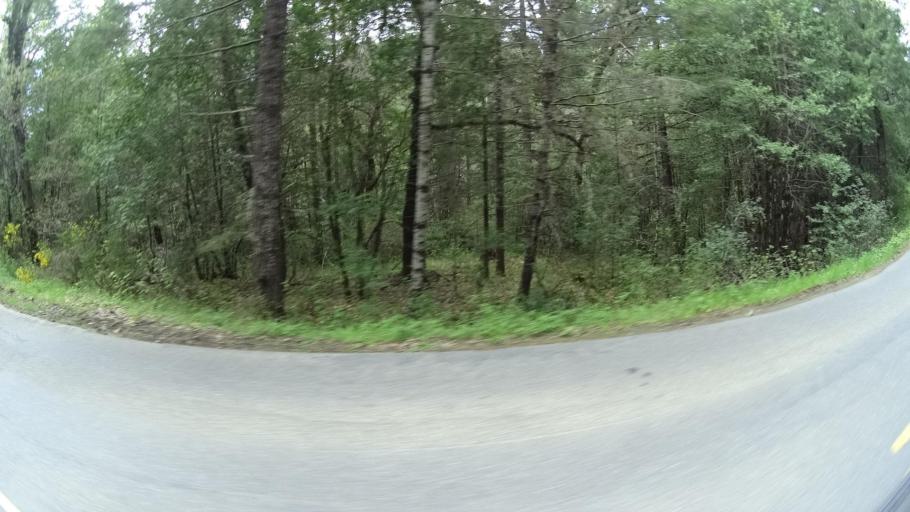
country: US
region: California
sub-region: Humboldt County
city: Redway
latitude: 40.1005
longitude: -123.9134
